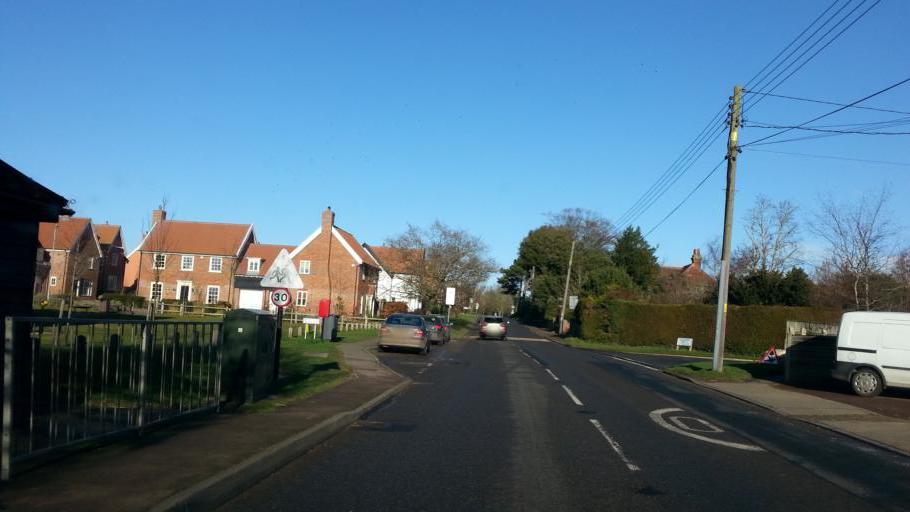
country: GB
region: England
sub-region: Suffolk
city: Saxmundham
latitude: 52.1718
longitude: 1.5010
